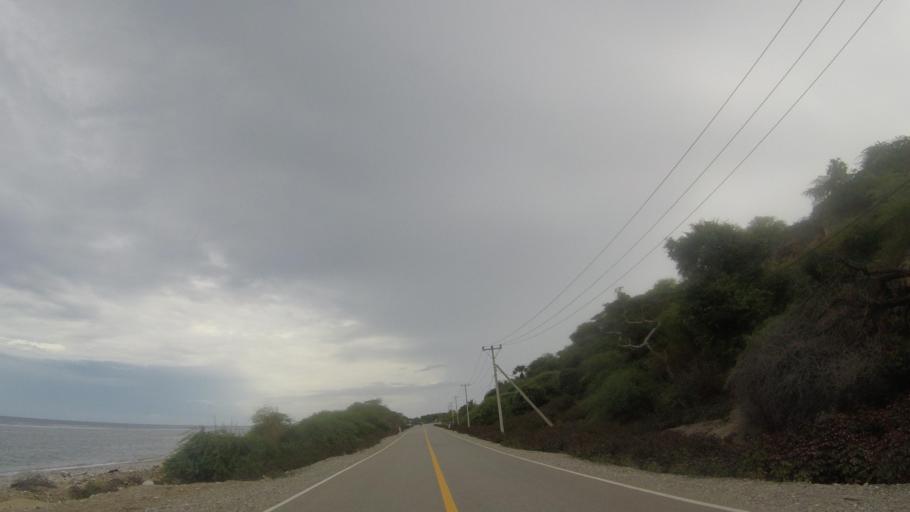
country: TL
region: Baucau
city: Baucau
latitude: -8.4094
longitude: 126.7215
